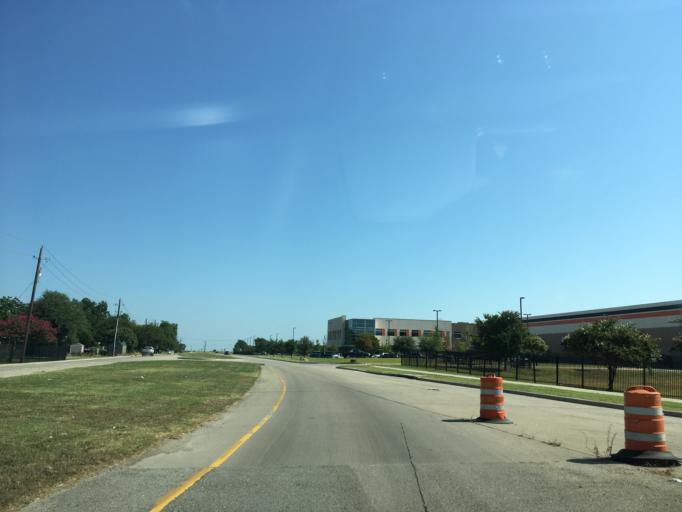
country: US
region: Texas
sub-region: Collin County
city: Fairview
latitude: 33.1673
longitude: -96.5987
